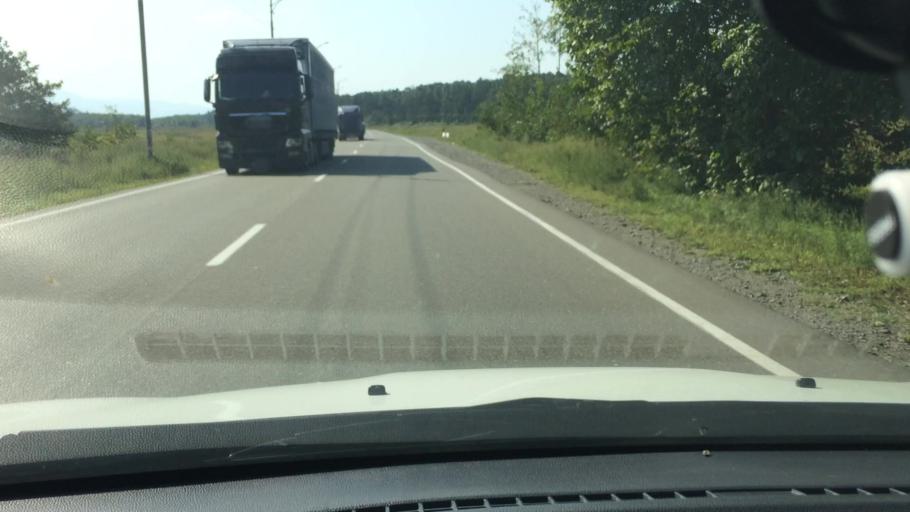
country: GE
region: Guria
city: Urek'i
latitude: 41.9561
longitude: 41.7716
